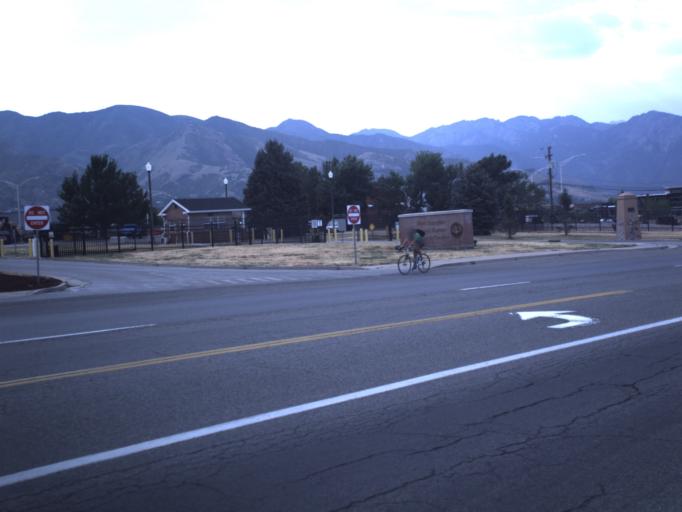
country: US
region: Utah
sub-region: Salt Lake County
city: Willard
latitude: 40.7595
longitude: -111.8348
